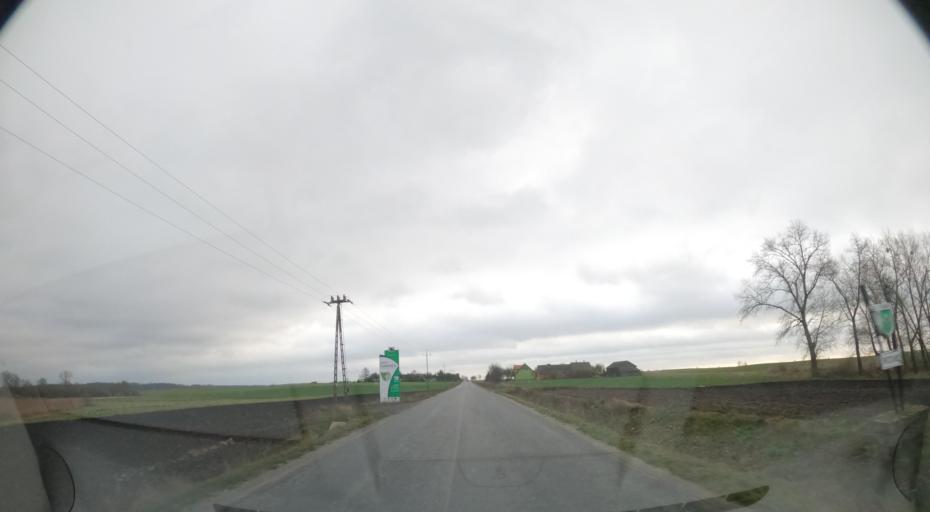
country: PL
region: Greater Poland Voivodeship
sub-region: Powiat pilski
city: Lobzenica
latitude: 53.2197
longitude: 17.3423
